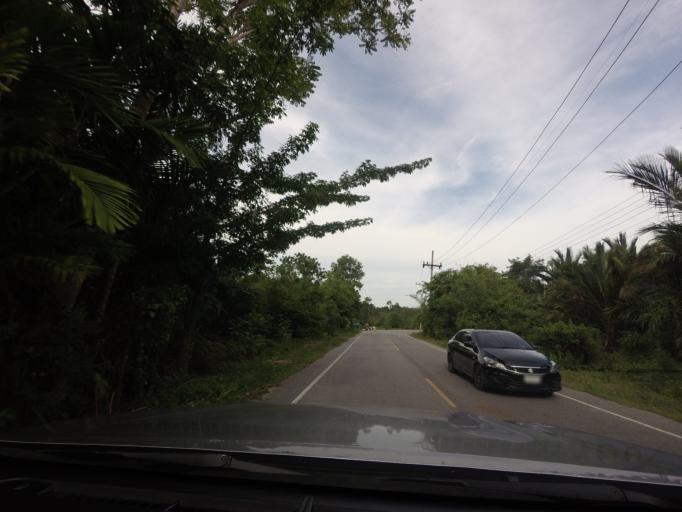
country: TH
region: Narathiwat
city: Rueso
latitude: 6.3470
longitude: 101.4784
